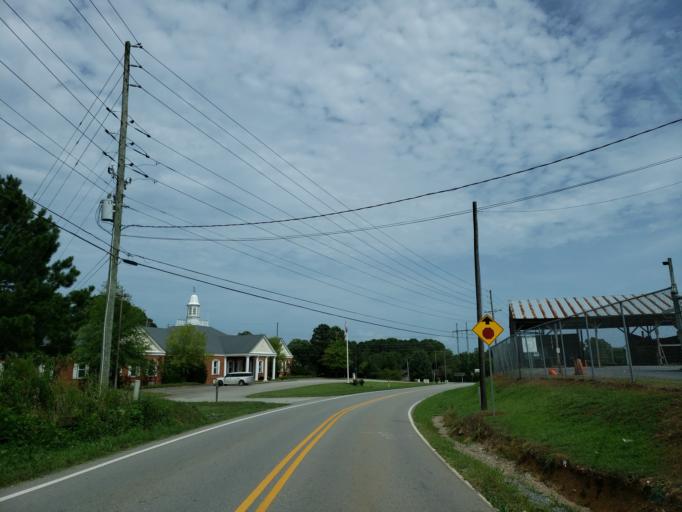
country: US
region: Georgia
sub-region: Pickens County
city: Jasper
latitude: 34.4564
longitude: -84.4492
